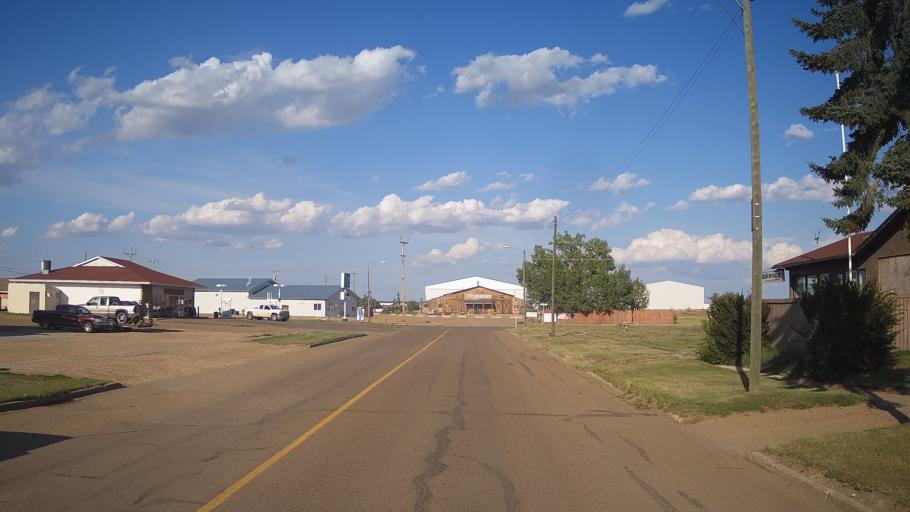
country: CA
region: Alberta
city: Hanna
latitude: 51.6447
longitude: -111.9199
